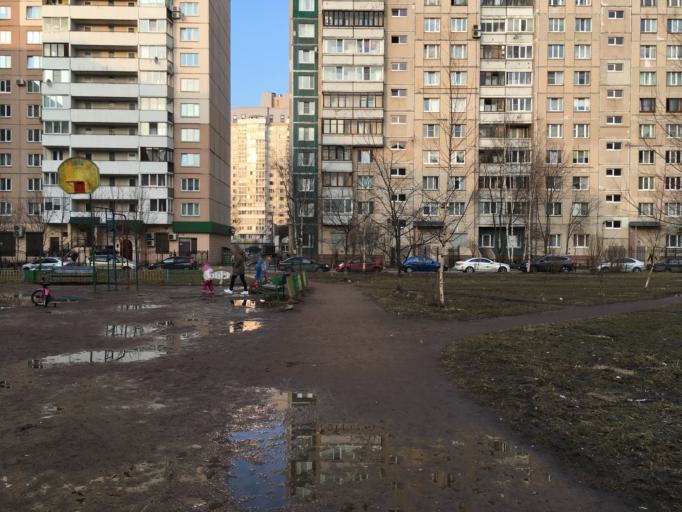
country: RU
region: St.-Petersburg
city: Komendantsky aerodrom
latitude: 60.0092
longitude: 30.2550
